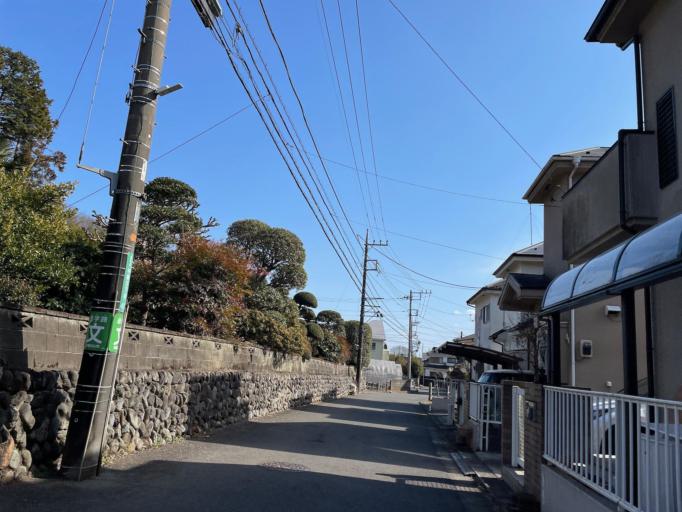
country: JP
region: Tokyo
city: Higashimurayama-shi
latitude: 35.7589
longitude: 139.3971
